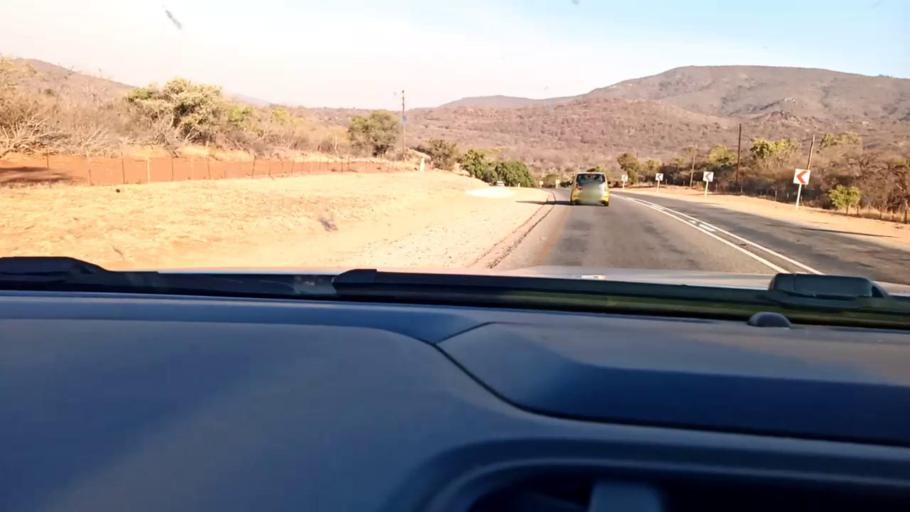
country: ZA
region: Limpopo
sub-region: Mopani District Municipality
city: Duiwelskloof
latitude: -23.6281
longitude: 30.1311
